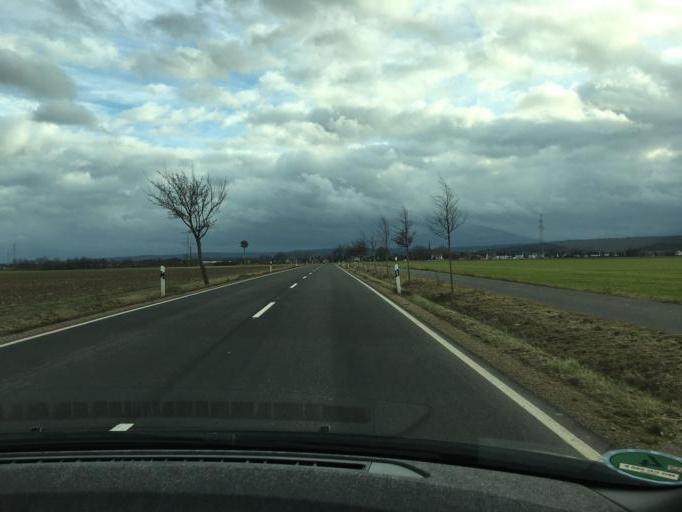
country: DE
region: North Rhine-Westphalia
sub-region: Regierungsbezirk Koln
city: Euskirchen
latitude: 50.6616
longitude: 6.7415
